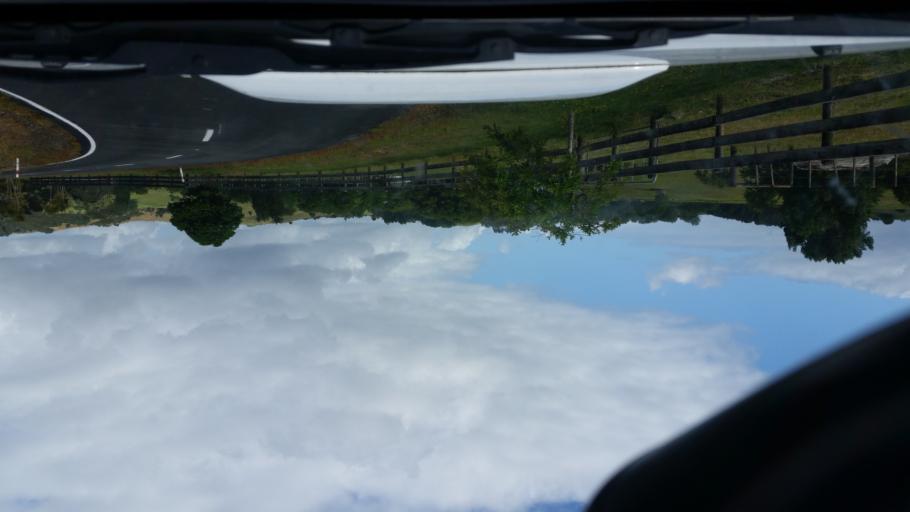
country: NZ
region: Auckland
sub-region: Auckland
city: Wellsford
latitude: -36.1316
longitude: 174.3654
